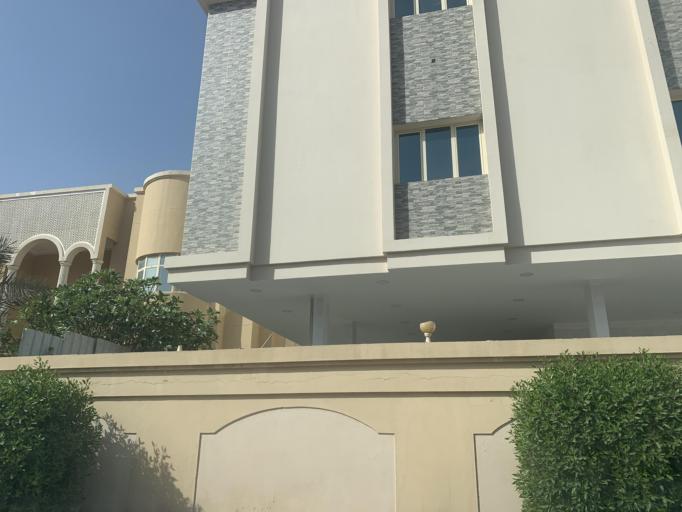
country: BH
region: Northern
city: Madinat `Isa
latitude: 26.1677
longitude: 50.5722
